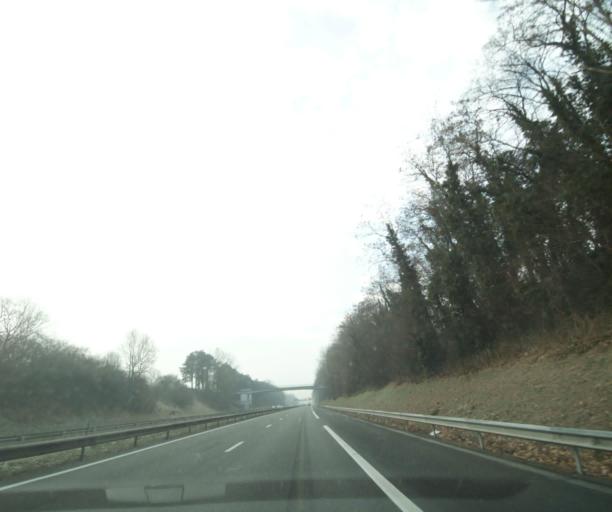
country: FR
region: Rhone-Alpes
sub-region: Departement du Rhone
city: Lissieu
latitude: 45.8764
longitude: 4.7398
